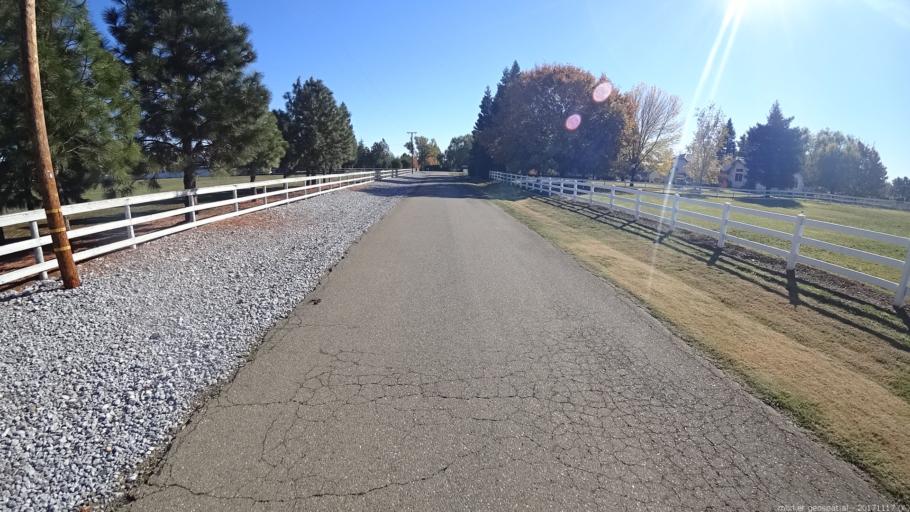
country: US
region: California
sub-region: Shasta County
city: Cottonwood
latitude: 40.4275
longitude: -122.2387
